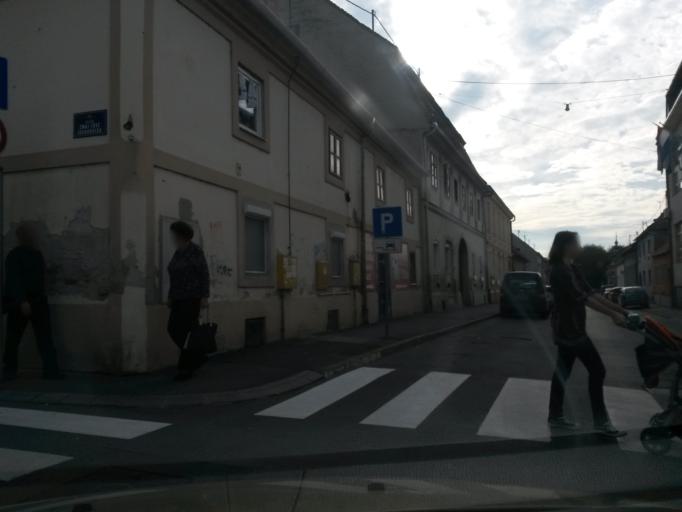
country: HR
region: Osjecko-Baranjska
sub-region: Grad Osijek
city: Osijek
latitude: 45.5588
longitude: 18.7192
